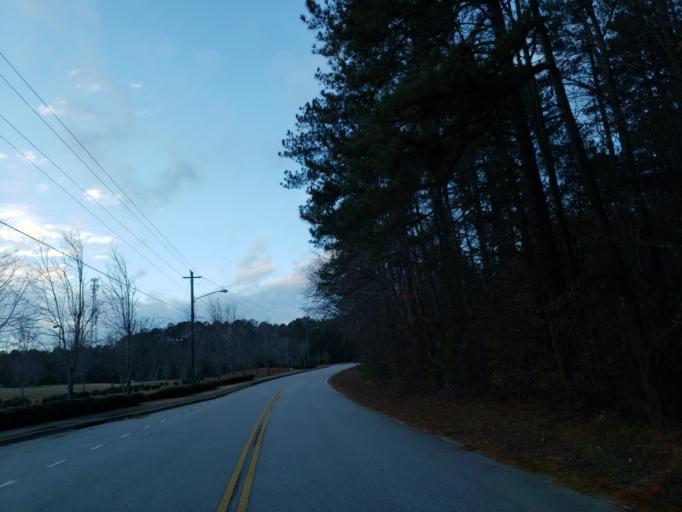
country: US
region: Georgia
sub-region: Fulton County
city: Union City
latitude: 33.6743
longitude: -84.5563
